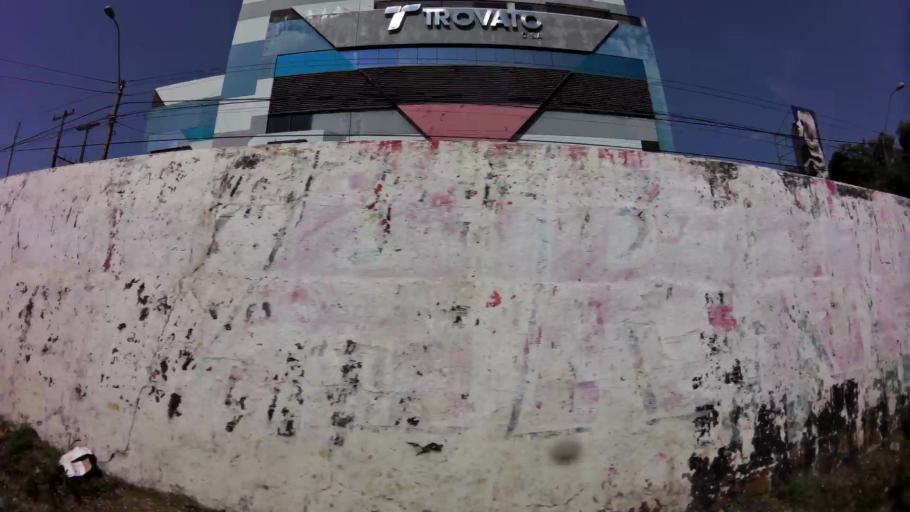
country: PY
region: Asuncion
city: Asuncion
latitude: -25.3030
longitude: -57.6323
